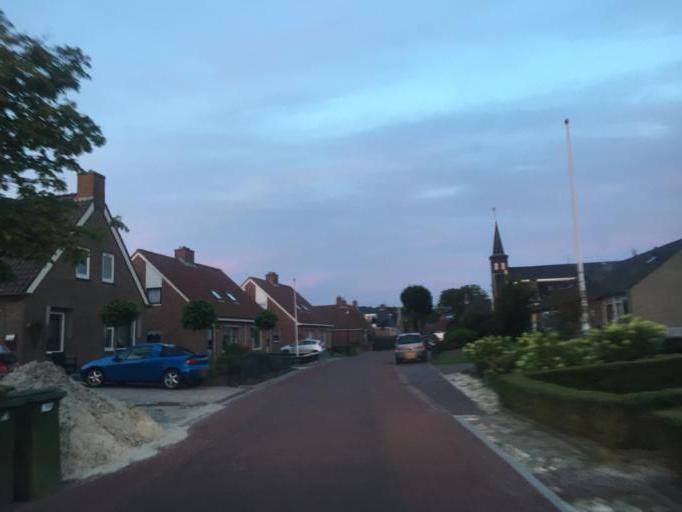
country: NL
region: Friesland
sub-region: Gemeente Dongeradeel
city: Anjum
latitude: 53.4034
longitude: 6.0808
